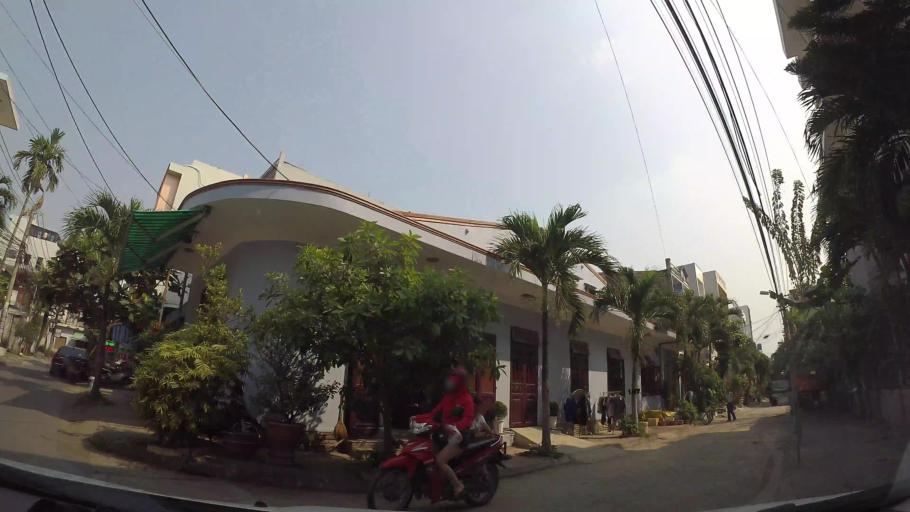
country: VN
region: Da Nang
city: Son Tra
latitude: 16.0426
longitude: 108.2417
